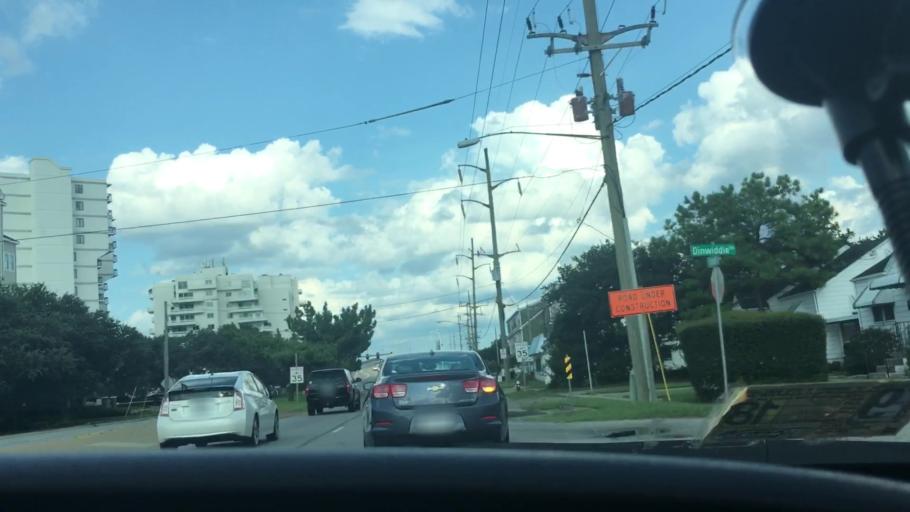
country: US
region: Virginia
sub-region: City of Virginia Beach
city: Virginia Beach
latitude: 36.9079
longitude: -76.0989
